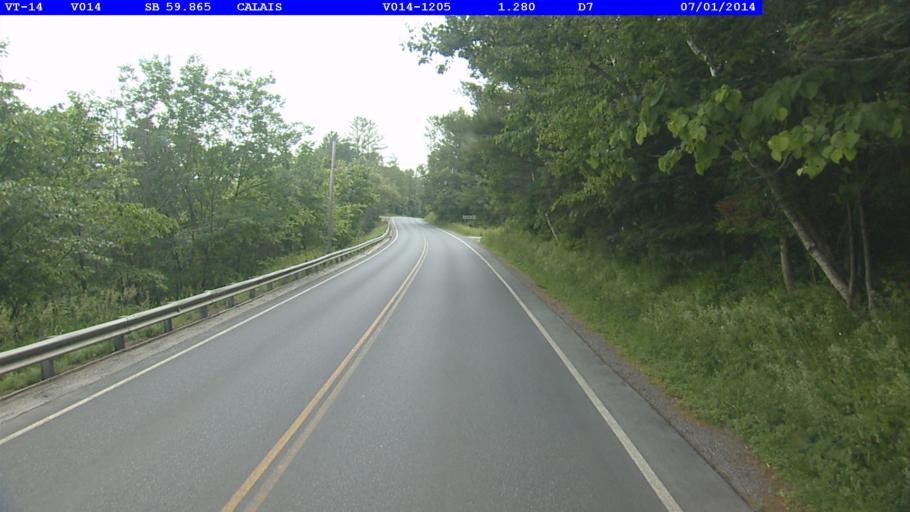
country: US
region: Vermont
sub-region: Washington County
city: Barre
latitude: 44.3255
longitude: -72.4439
